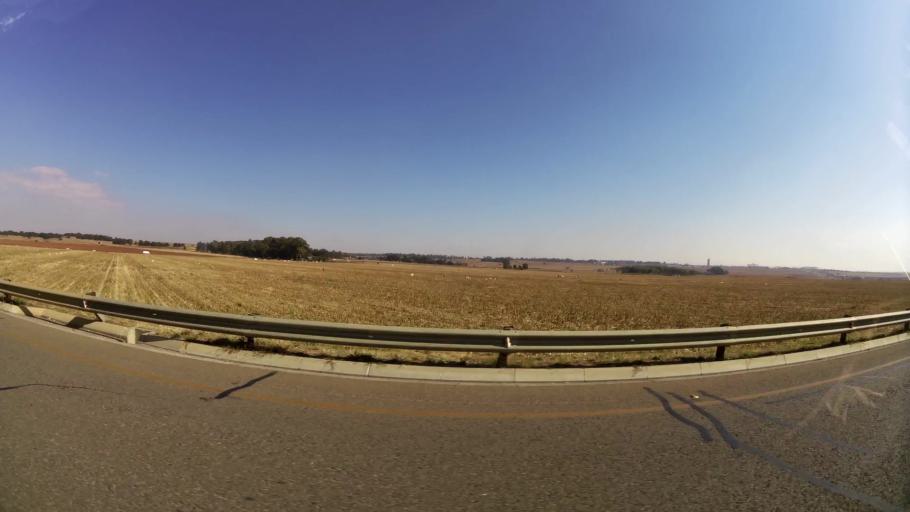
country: ZA
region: Gauteng
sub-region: Ekurhuleni Metropolitan Municipality
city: Tembisa
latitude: -26.0561
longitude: 28.2807
